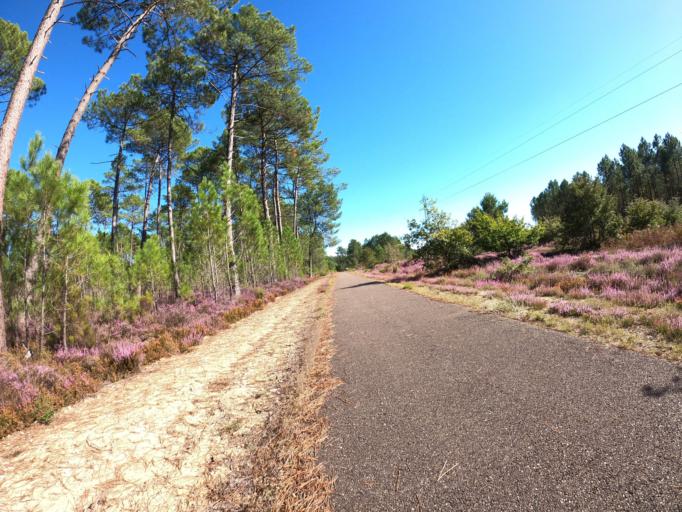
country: FR
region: Aquitaine
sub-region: Departement des Landes
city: Ychoux
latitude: 44.3368
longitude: -0.9517
